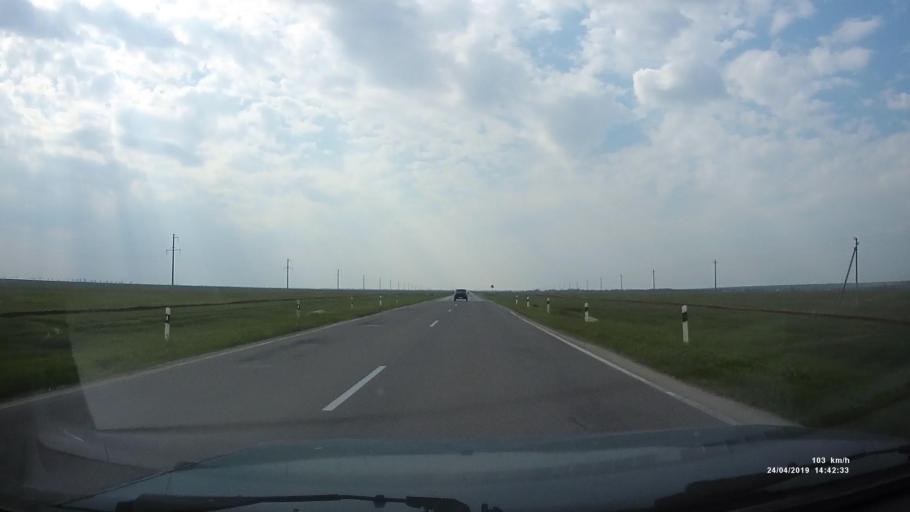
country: RU
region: Rostov
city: Remontnoye
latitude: 46.4526
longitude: 43.8594
